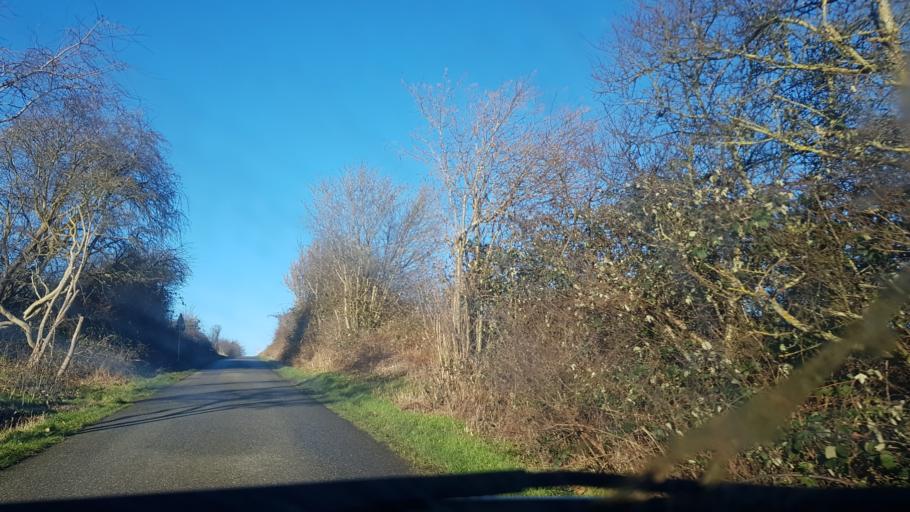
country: DK
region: South Denmark
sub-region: Fredericia Kommune
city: Taulov
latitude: 55.5289
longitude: 9.6452
